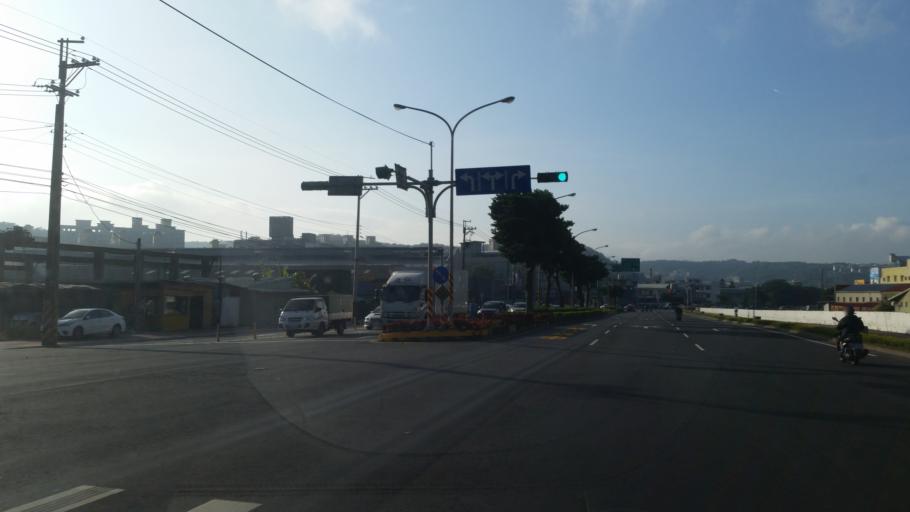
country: TW
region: Taiwan
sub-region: Taoyuan
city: Taoyuan
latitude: 25.0040
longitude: 121.3440
